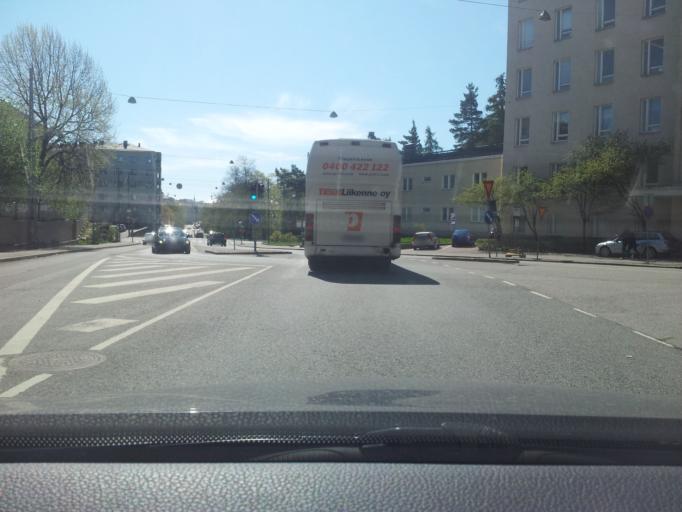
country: FI
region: Uusimaa
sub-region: Helsinki
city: Helsinki
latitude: 60.1895
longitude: 24.9120
